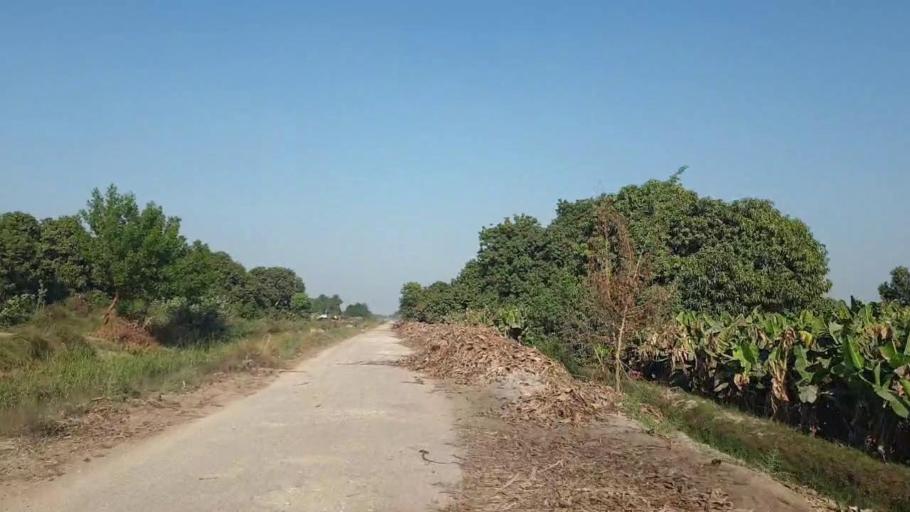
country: PK
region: Sindh
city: Matiari
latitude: 25.5335
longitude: 68.4366
